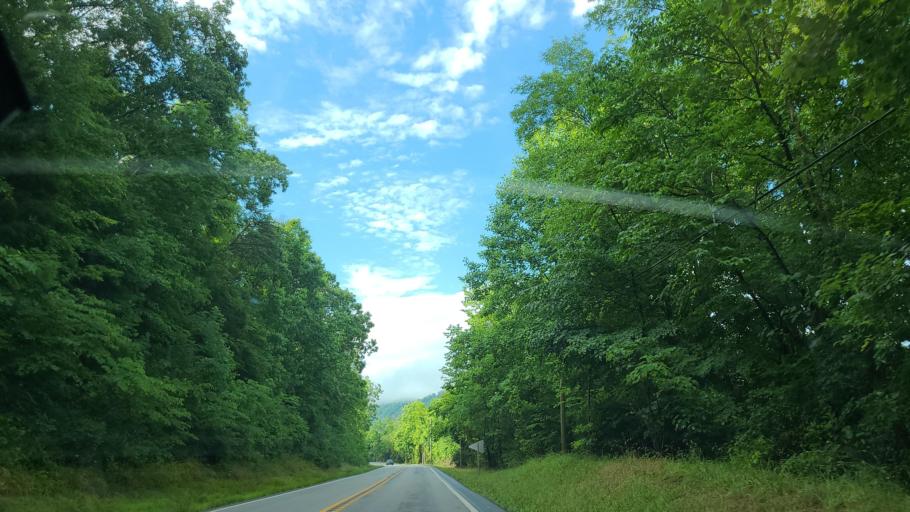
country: US
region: Kentucky
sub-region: Whitley County
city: Williamsburg
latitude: 36.7319
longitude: -84.1297
